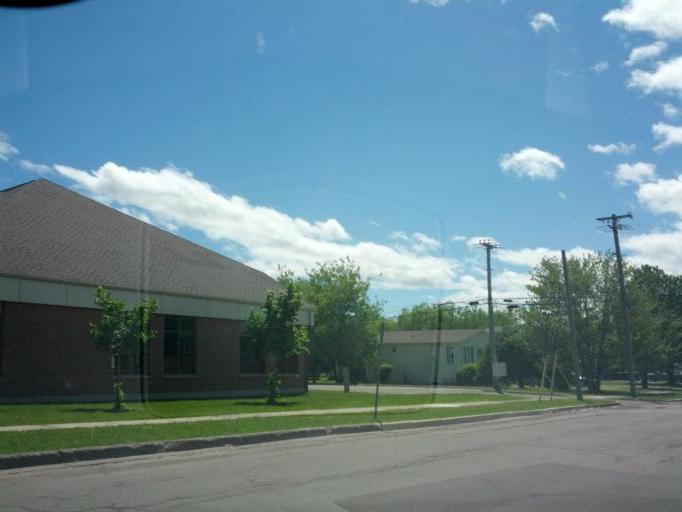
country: CA
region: New Brunswick
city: Moncton
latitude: 46.1152
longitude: -64.7739
